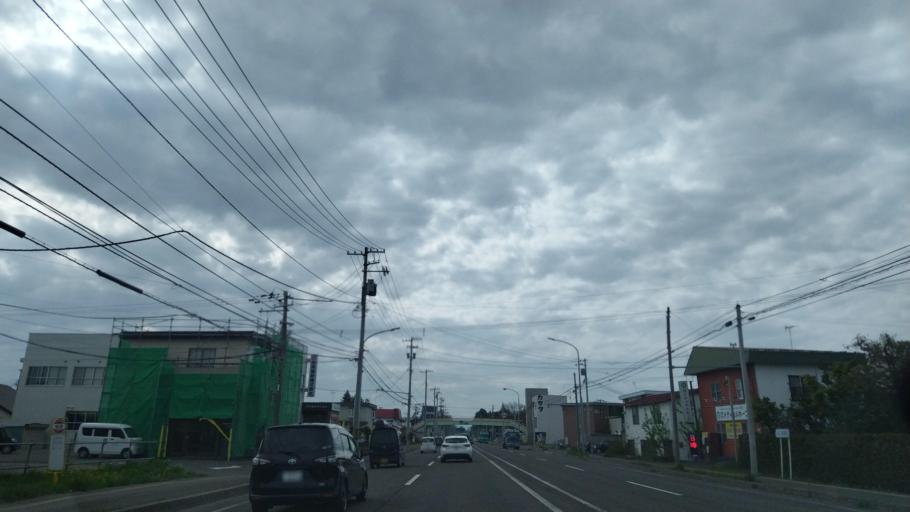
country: JP
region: Hokkaido
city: Obihiro
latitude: 42.9283
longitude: 143.2168
